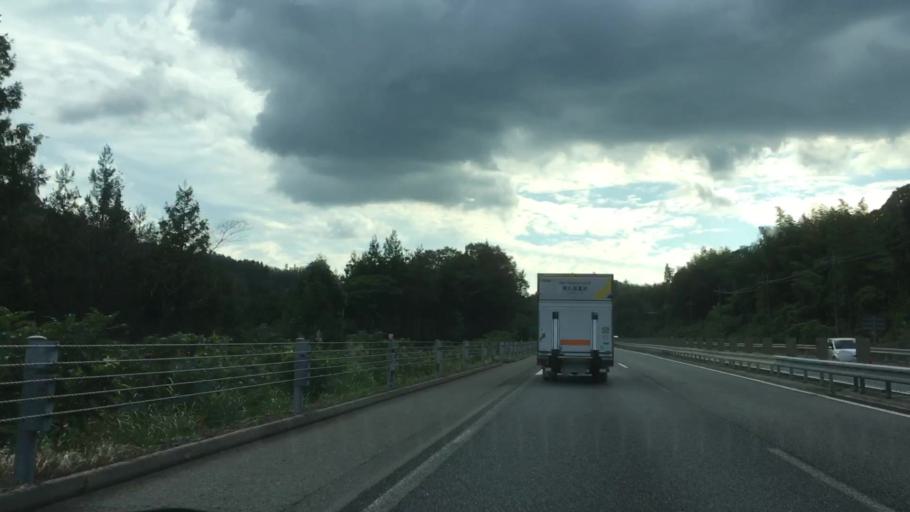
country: JP
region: Yamaguchi
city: Iwakuni
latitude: 34.1352
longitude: 132.1157
